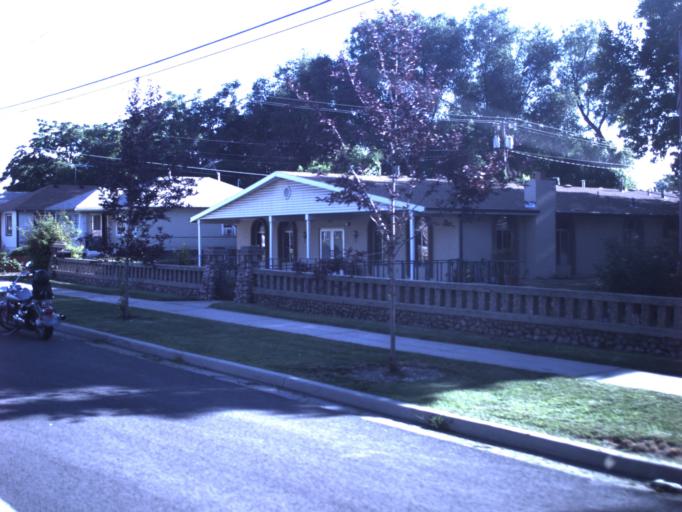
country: US
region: Utah
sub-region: Utah County
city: Springville
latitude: 40.1733
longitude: -111.6107
